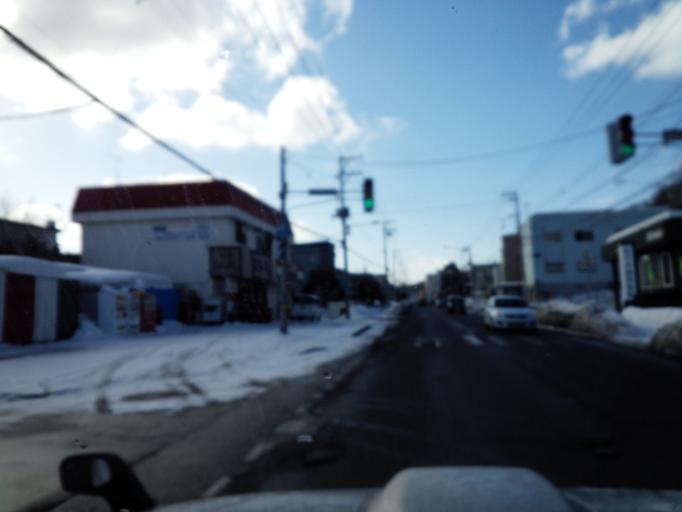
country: JP
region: Hokkaido
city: Sapporo
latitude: 42.9605
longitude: 141.3434
